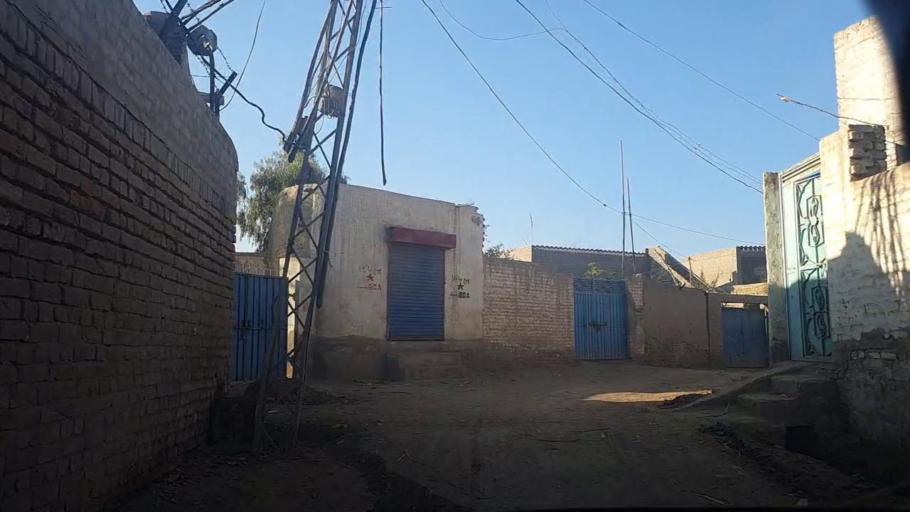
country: PK
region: Sindh
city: Sobhadero
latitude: 27.3989
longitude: 68.4211
